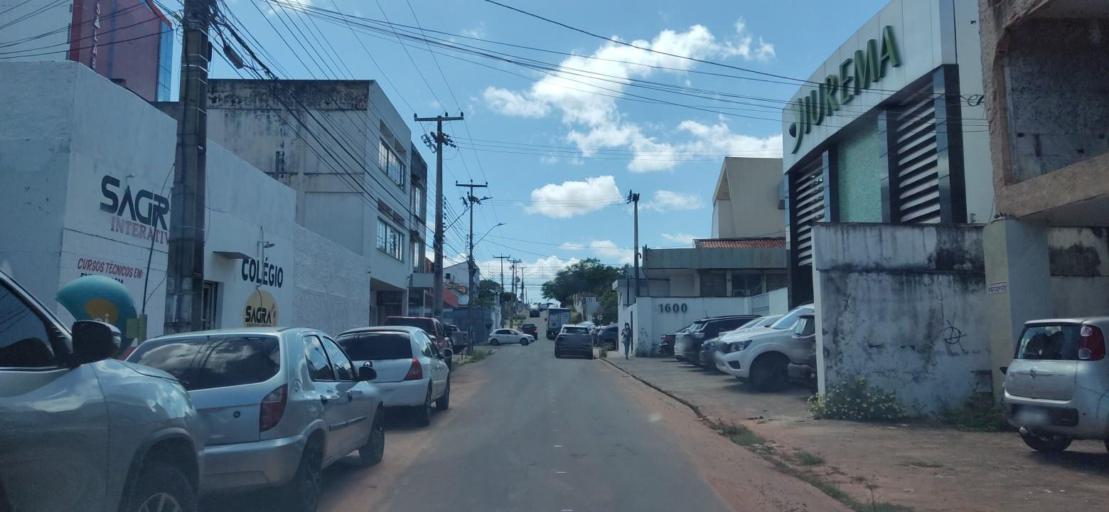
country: BR
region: Piaui
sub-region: Teresina
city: Teresina
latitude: -5.0879
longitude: -42.8119
